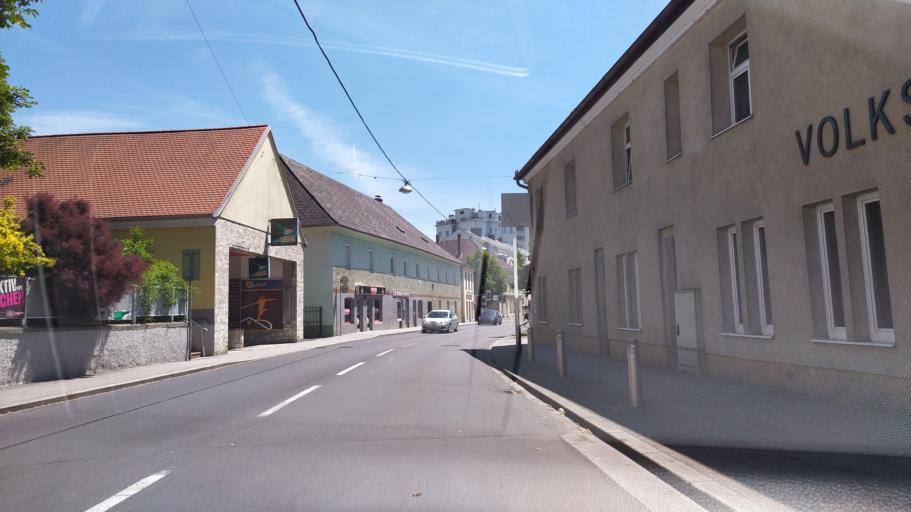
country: AT
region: Upper Austria
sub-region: Politischer Bezirk Linz-Land
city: Ansfelden
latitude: 48.2532
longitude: 14.3131
